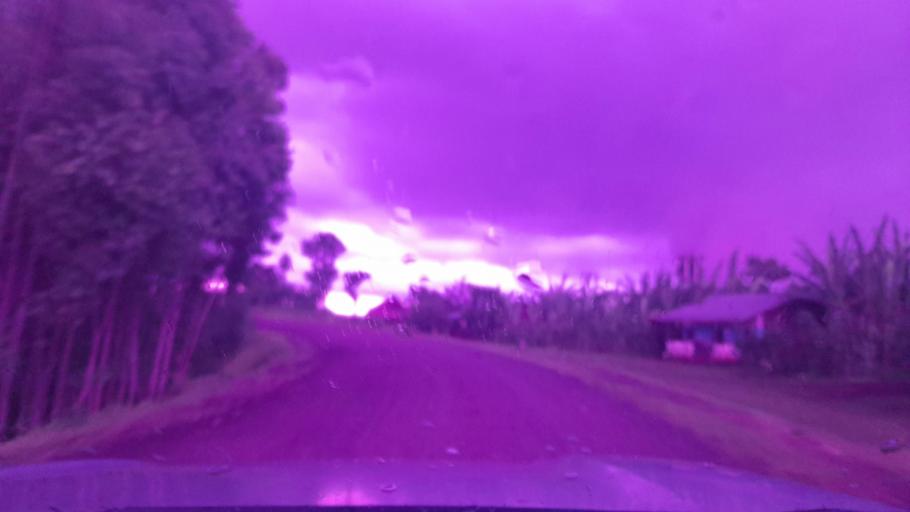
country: ET
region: Southern Nations, Nationalities, and People's Region
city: Mizan Teferi
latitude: 6.9144
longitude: 35.8429
